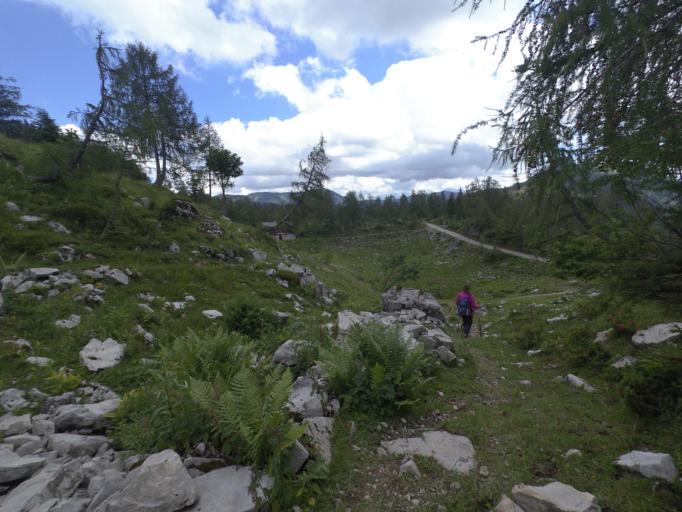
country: AT
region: Salzburg
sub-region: Politischer Bezirk Salzburg-Umgebung
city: Hintersee
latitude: 47.6616
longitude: 13.3017
